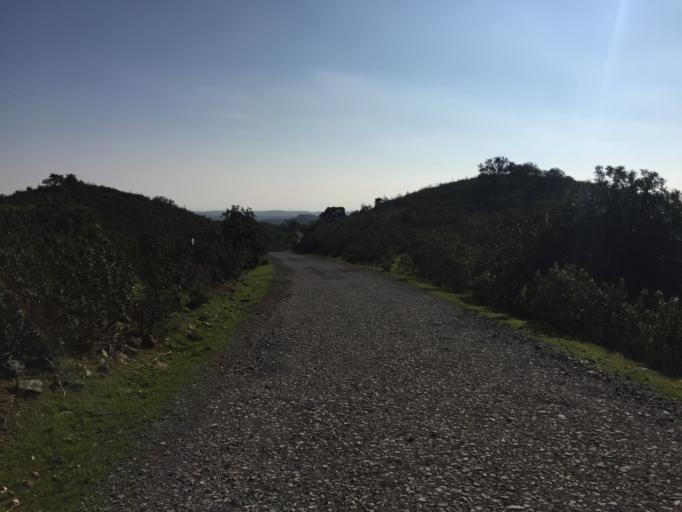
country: PT
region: Faro
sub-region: Castro Marim
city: Castro Marim
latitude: 37.2375
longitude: -7.5654
